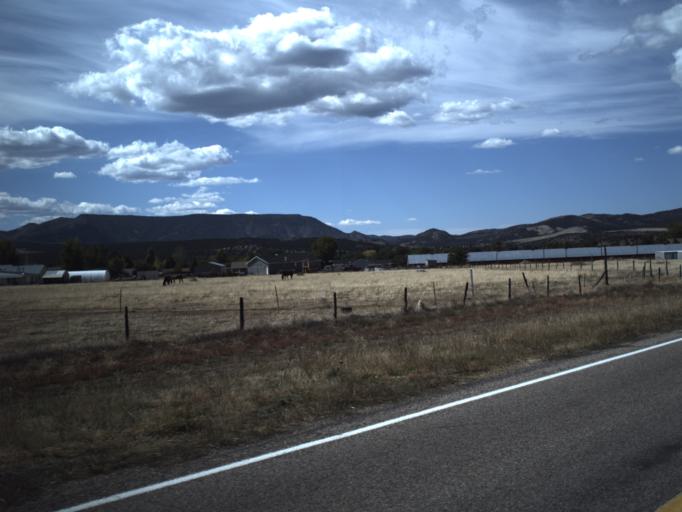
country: US
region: Utah
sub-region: Washington County
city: Enterprise
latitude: 37.5714
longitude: -113.7029
